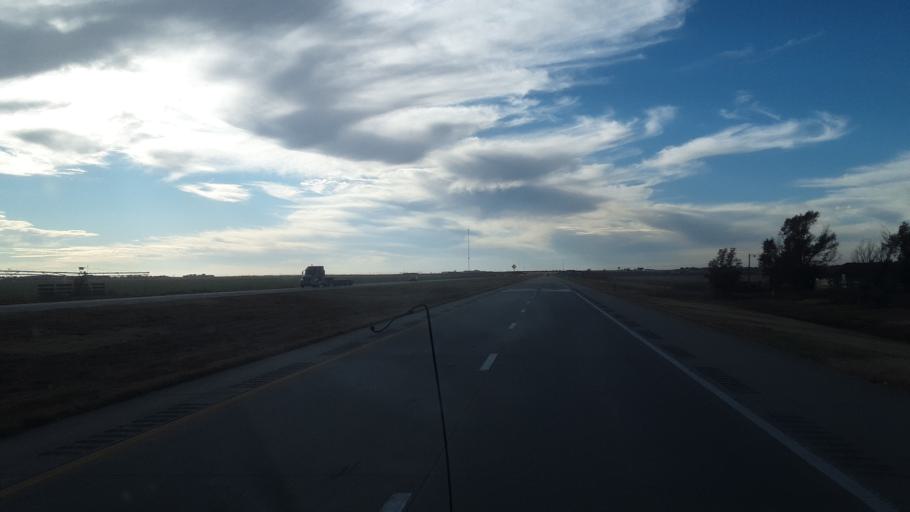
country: US
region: Kansas
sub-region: Finney County
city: Holcomb
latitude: 38.0034
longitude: -100.9742
